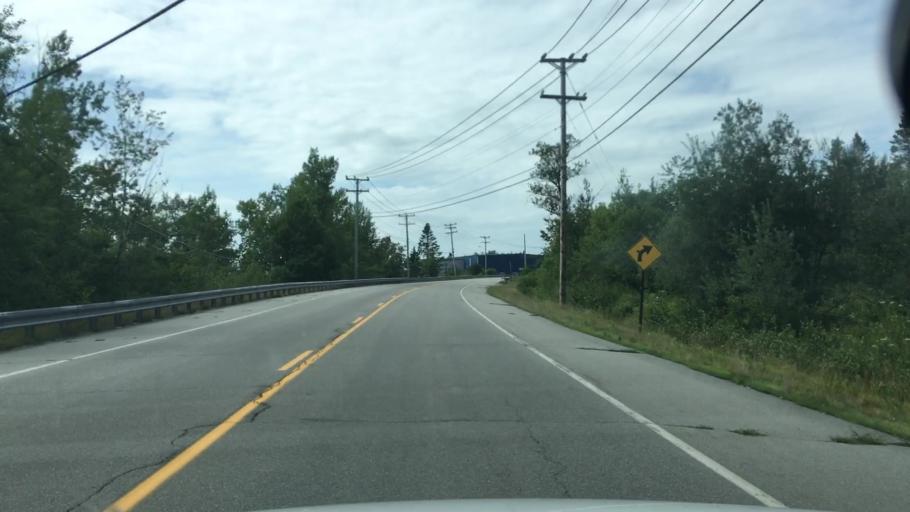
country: US
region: Maine
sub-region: Washington County
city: Eastport
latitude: 44.9263
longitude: -67.0218
